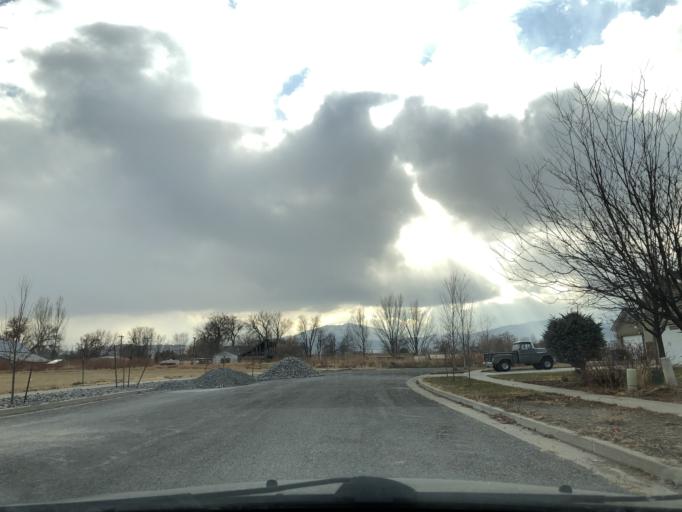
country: US
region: Utah
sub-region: Cache County
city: Wellsville
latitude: 41.6499
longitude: -111.9116
